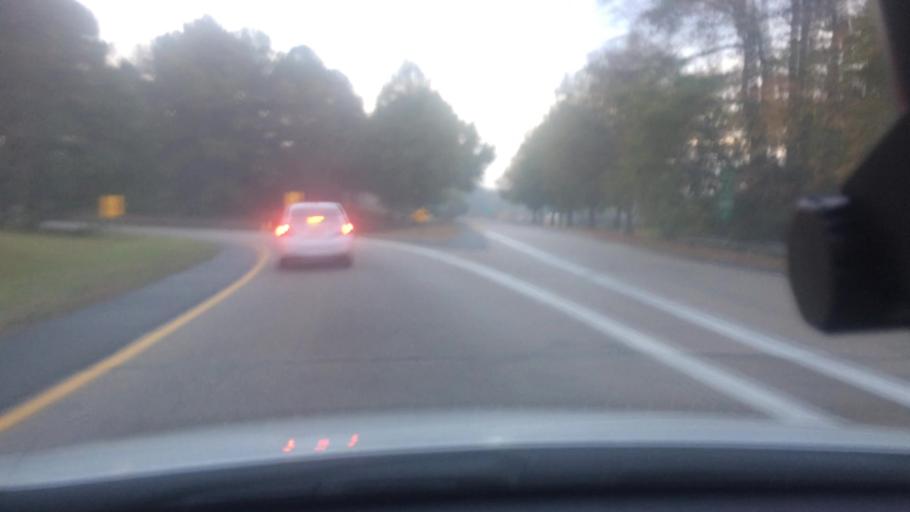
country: US
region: North Carolina
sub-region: Wake County
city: Raleigh
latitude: 35.8154
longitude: -78.6076
